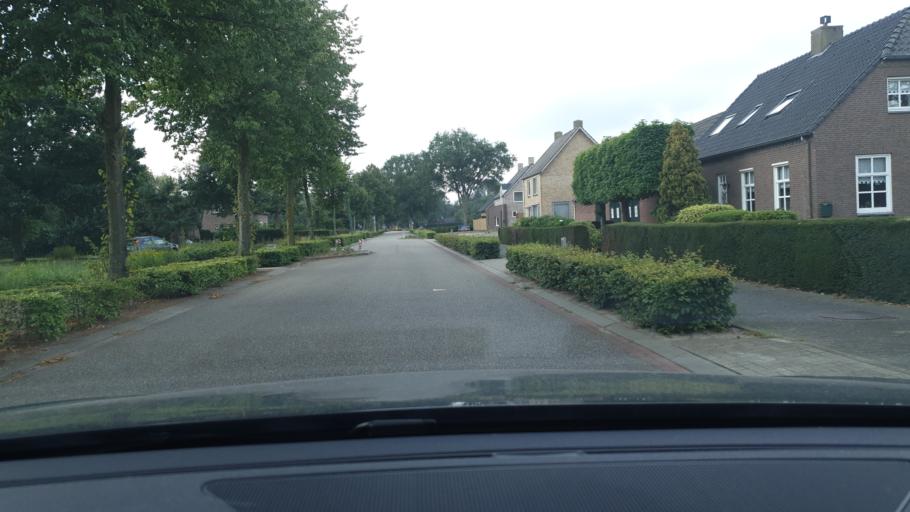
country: NL
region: North Brabant
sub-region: Gemeente Veldhoven
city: Oerle
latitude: 51.4412
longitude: 5.3312
